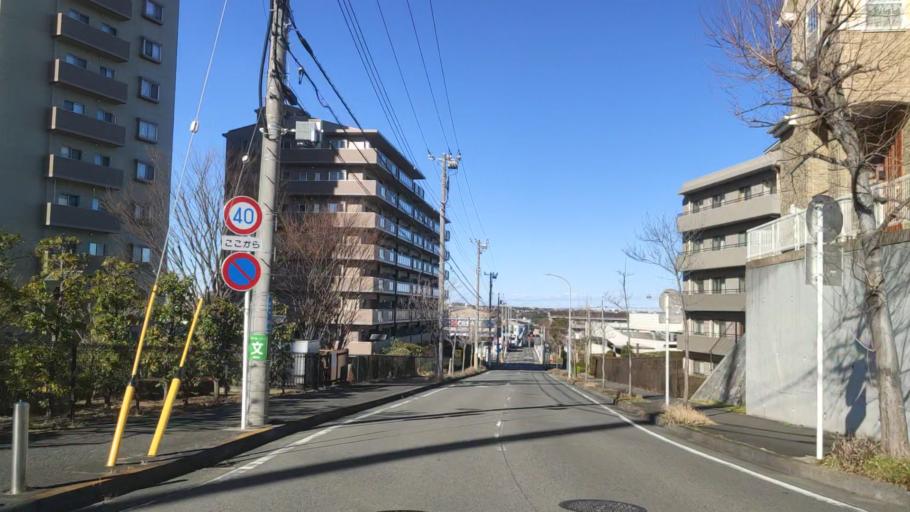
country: JP
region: Kanagawa
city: Minami-rinkan
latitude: 35.5067
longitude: 139.5344
